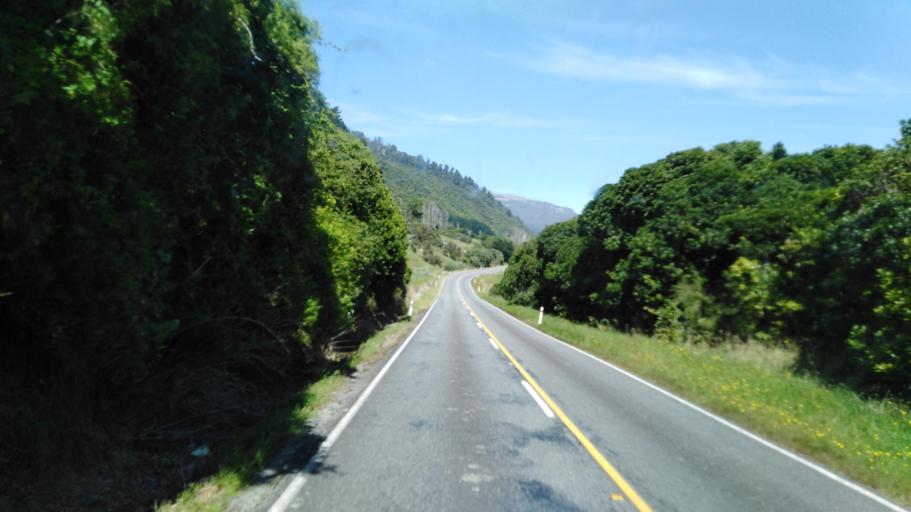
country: NZ
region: West Coast
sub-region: Buller District
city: Westport
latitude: -41.5775
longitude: 171.9002
